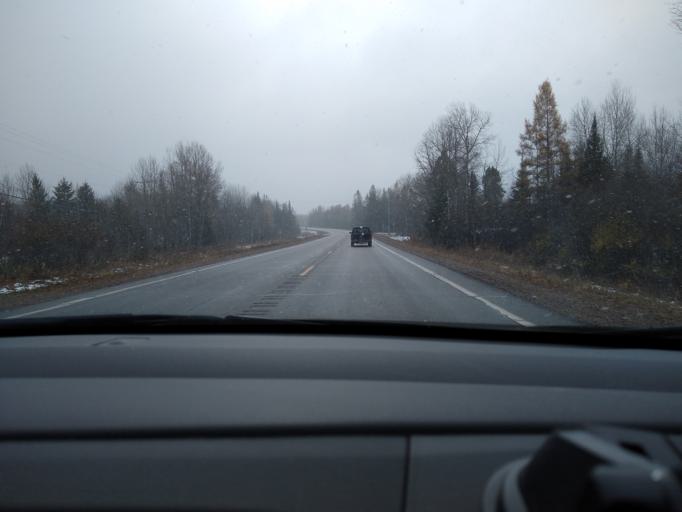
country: US
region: Wisconsin
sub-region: Florence County
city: Florence
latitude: 46.0743
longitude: -88.0760
